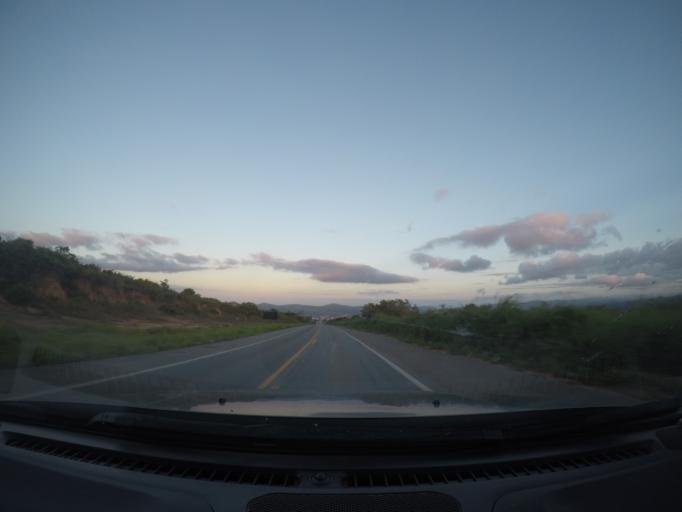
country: BR
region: Bahia
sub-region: Seabra
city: Seabra
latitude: -12.4339
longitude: -41.8196
